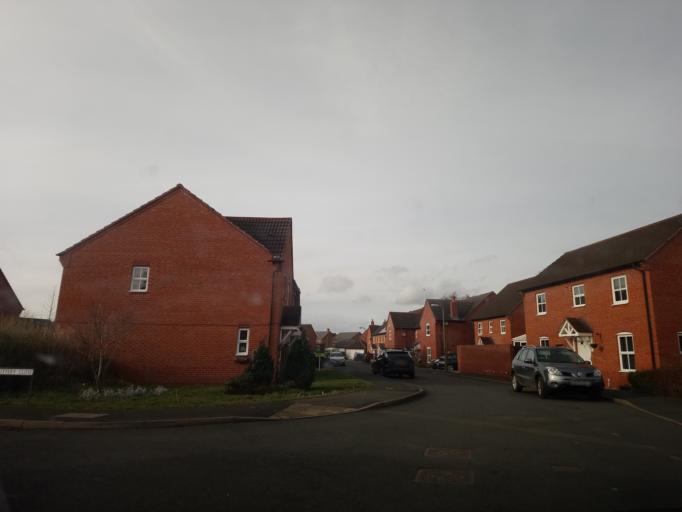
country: GB
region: England
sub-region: Shropshire
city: Wem
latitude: 52.8627
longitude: -2.7148
